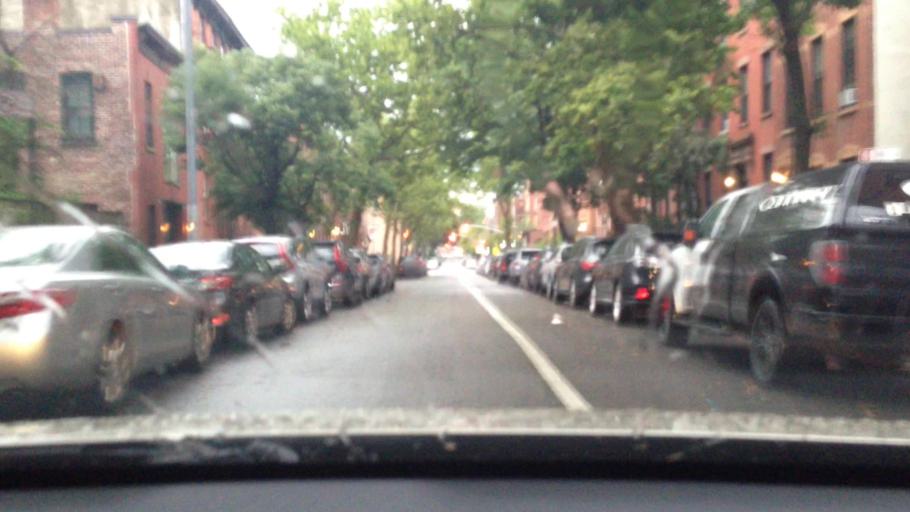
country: US
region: New York
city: New York City
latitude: 40.6867
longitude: -73.9983
